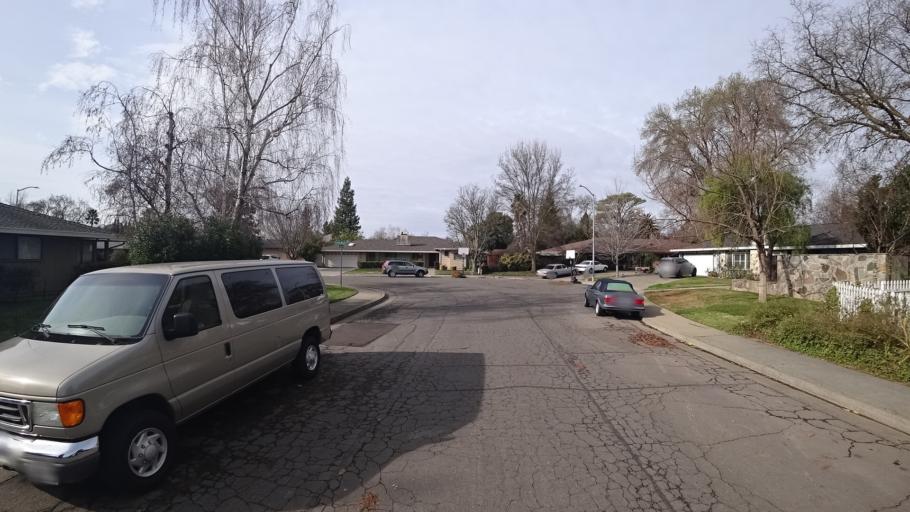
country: US
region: California
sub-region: Yolo County
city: Davis
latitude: 38.5455
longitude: -121.6976
